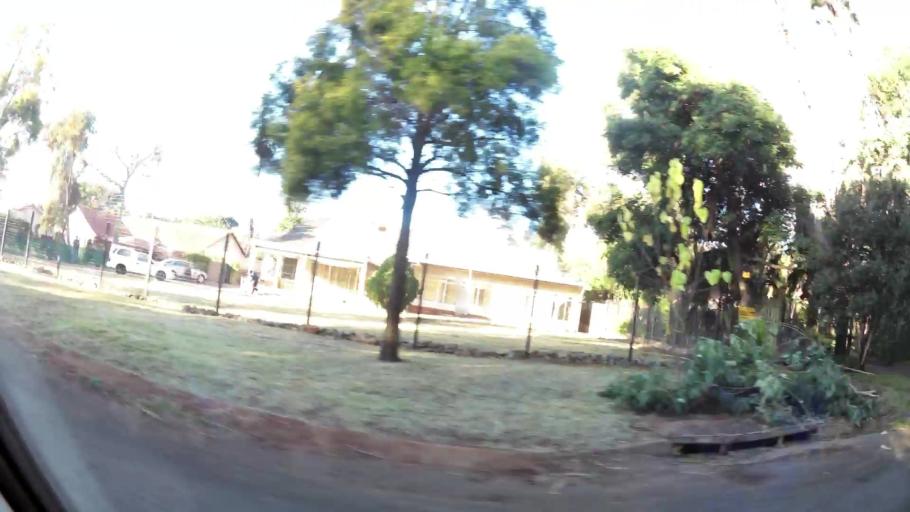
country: ZA
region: North-West
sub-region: Bojanala Platinum District Municipality
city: Rustenburg
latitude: -25.6890
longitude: 27.2053
